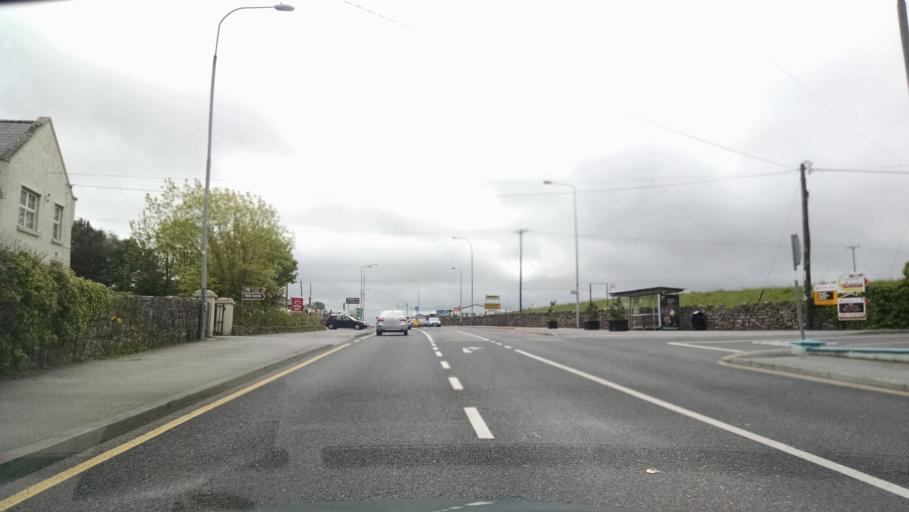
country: IE
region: Connaught
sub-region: County Galway
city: Oranmore
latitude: 53.2116
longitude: -8.8703
